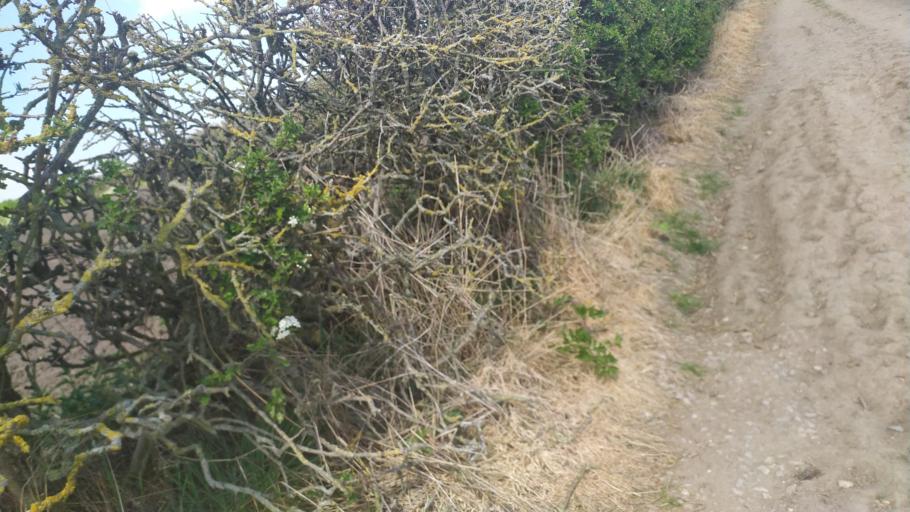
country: GB
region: England
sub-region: City and Borough of Leeds
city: Chapel Allerton
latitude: 53.8725
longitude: -1.5632
